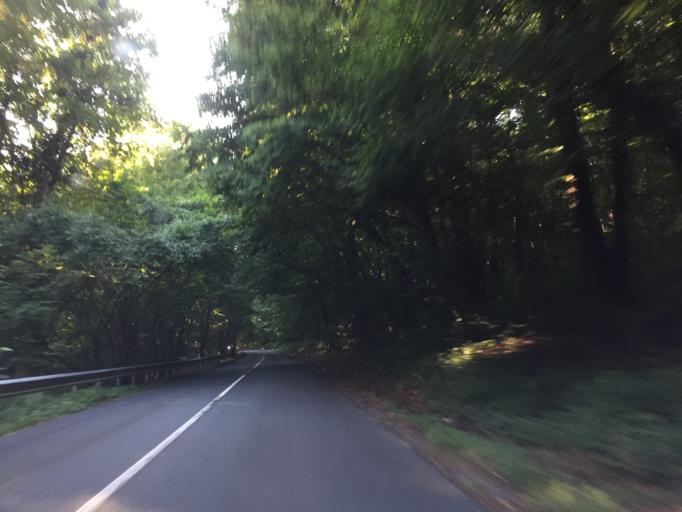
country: FR
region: Lower Normandy
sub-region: Departement du Calvados
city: Equemauville
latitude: 49.3940
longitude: 0.1897
